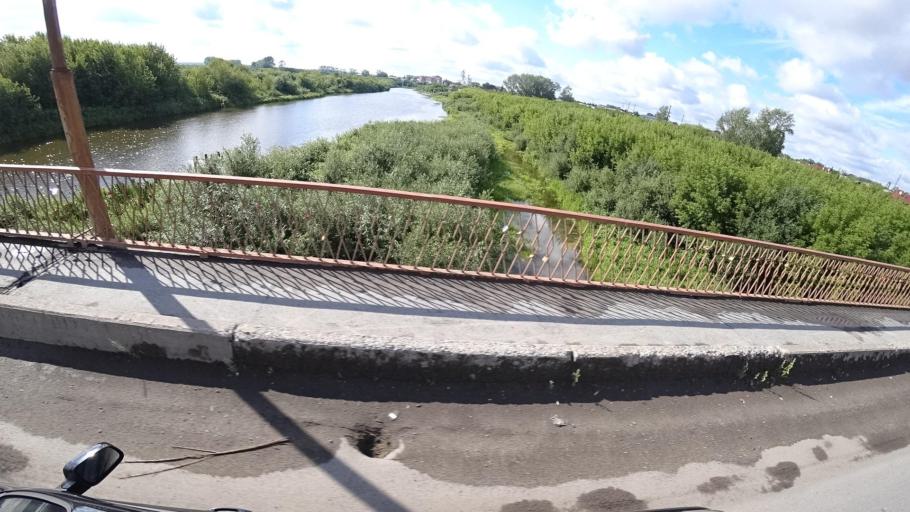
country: RU
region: Sverdlovsk
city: Kamyshlov
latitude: 56.8399
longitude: 62.7033
